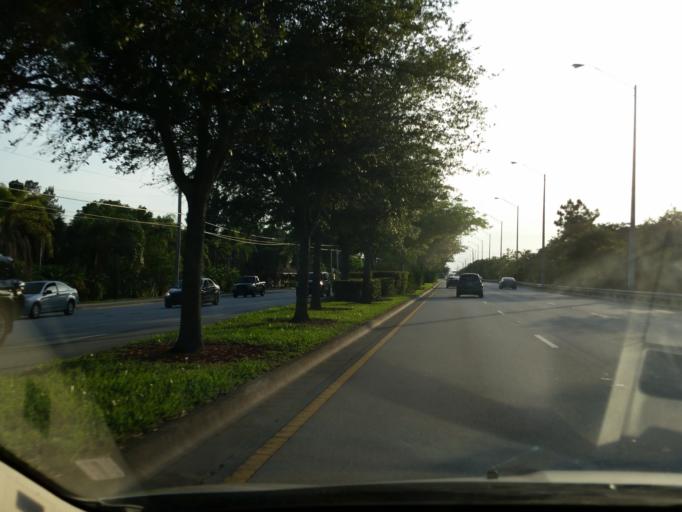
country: US
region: Florida
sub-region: Broward County
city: Davie
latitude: 26.0650
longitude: -80.2409
